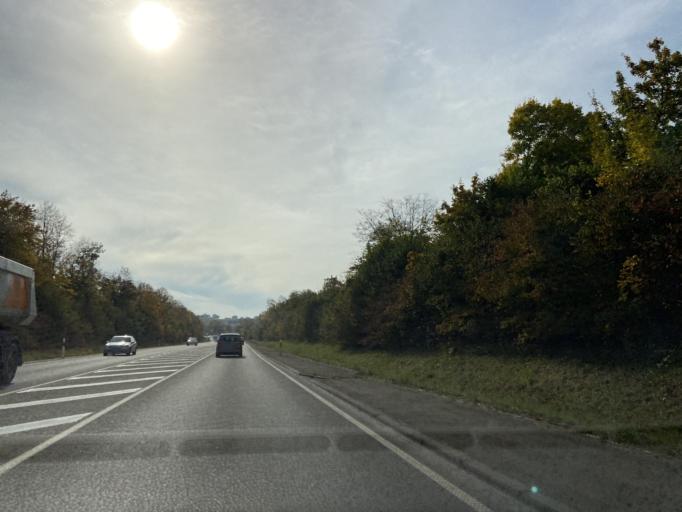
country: DE
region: Baden-Wuerttemberg
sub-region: Tuebingen Region
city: Sigmaringen
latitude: 48.0820
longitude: 9.2066
